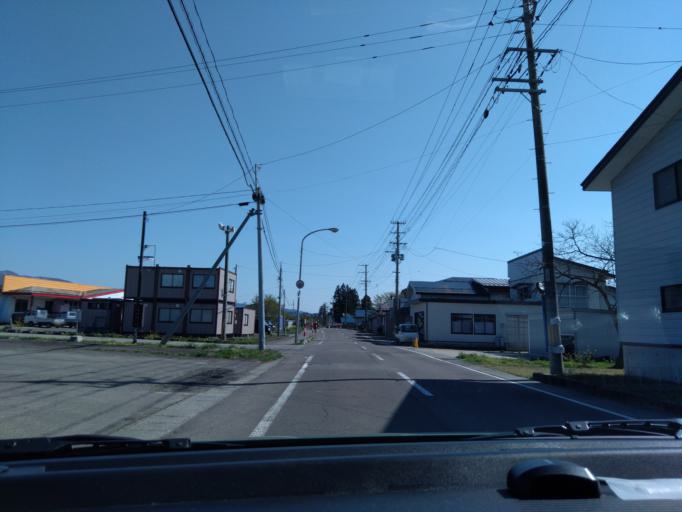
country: JP
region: Akita
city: Kakunodatemachi
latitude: 39.4960
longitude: 140.5940
